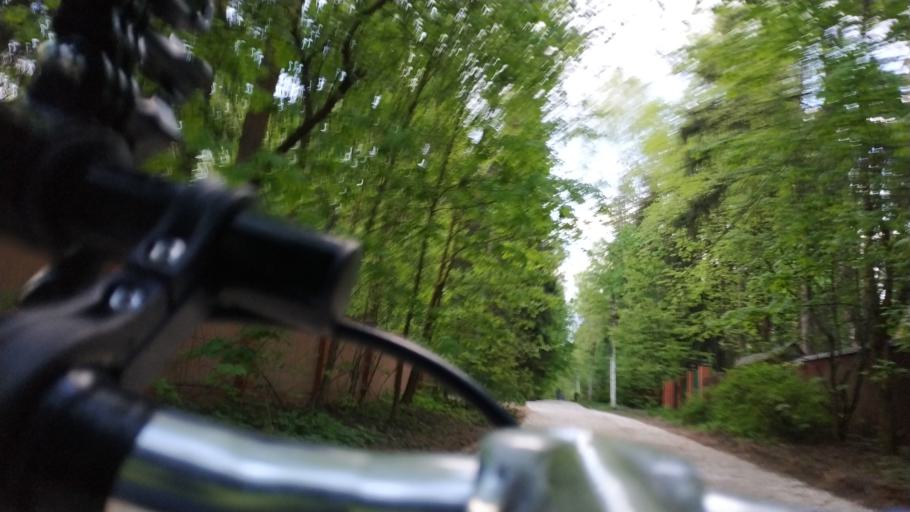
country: RU
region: Moskovskaya
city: Kratovo
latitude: 55.5969
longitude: 38.1593
